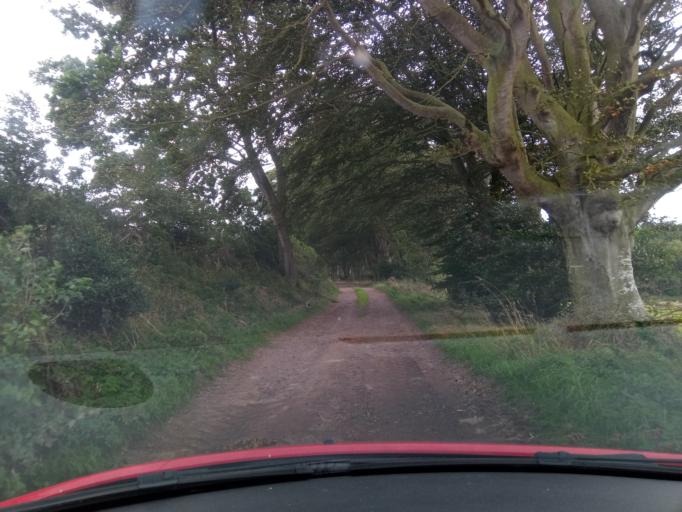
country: GB
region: Scotland
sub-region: The Scottish Borders
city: Jedburgh
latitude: 55.4890
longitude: -2.5233
